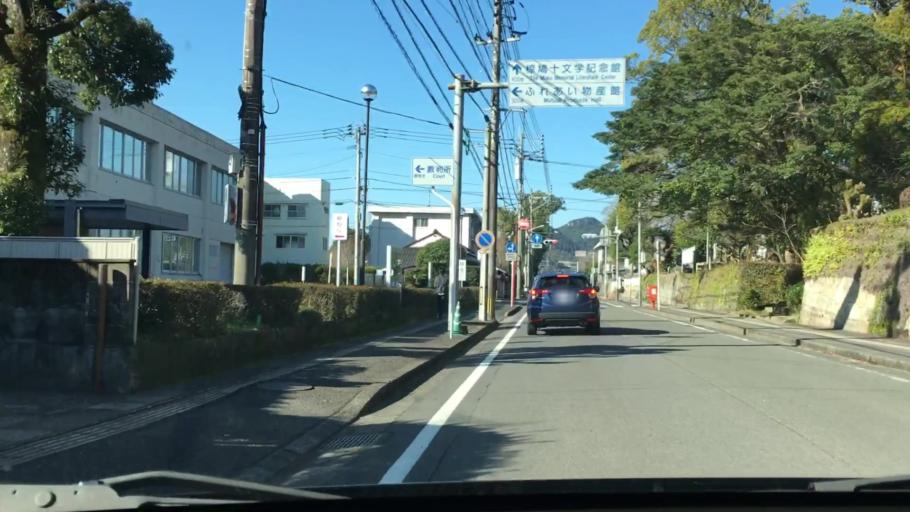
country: JP
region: Kagoshima
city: Kajiki
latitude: 31.7409
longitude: 130.6660
